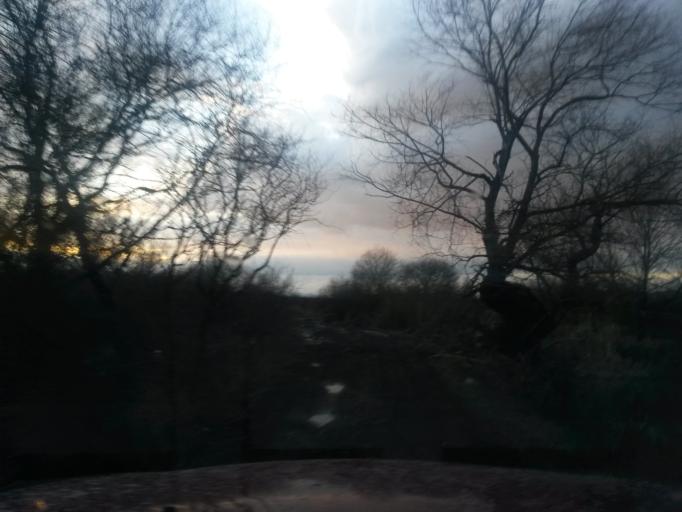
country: SK
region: Kosicky
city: Sobrance
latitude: 48.7029
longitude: 22.0707
